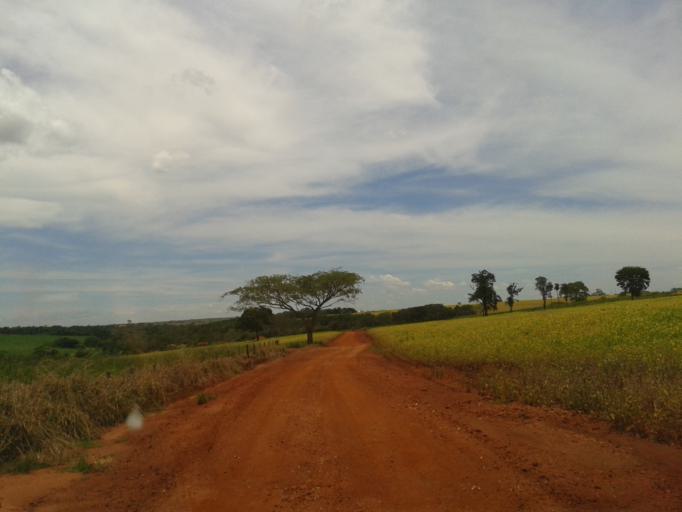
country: BR
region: Minas Gerais
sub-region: Capinopolis
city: Capinopolis
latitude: -18.6793
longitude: -49.7188
